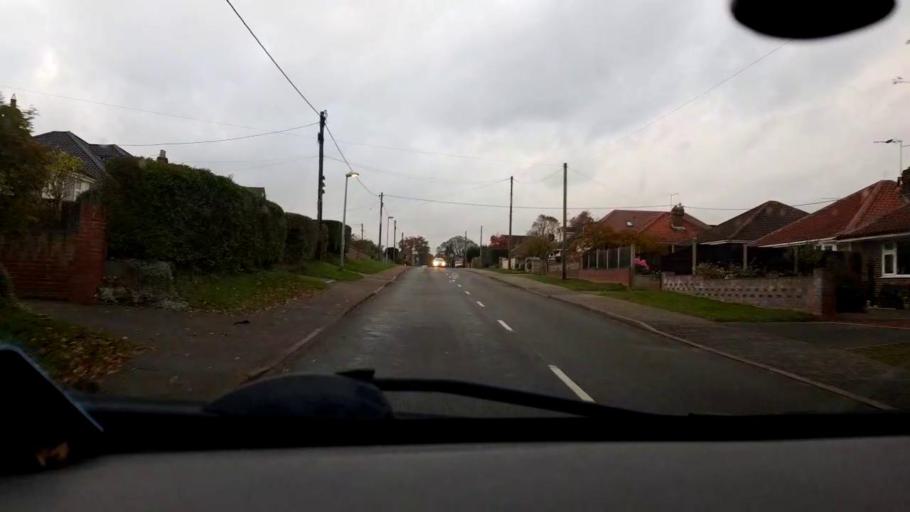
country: GB
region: England
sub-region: Norfolk
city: Spixworth
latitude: 52.6877
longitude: 1.3211
